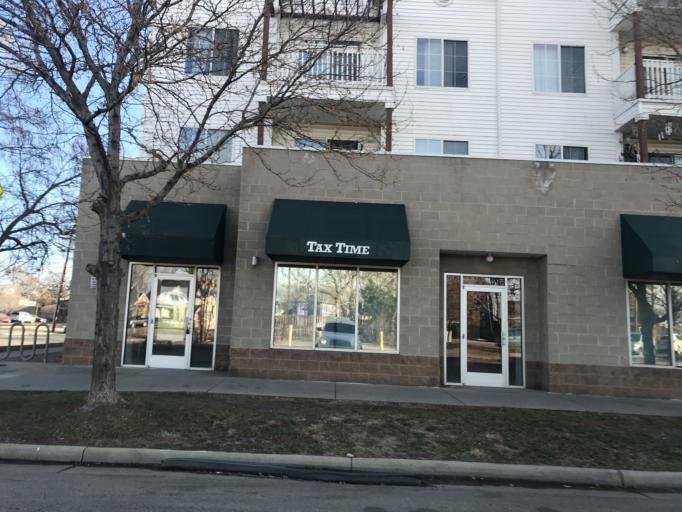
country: US
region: Colorado
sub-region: Denver County
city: Denver
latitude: 39.7631
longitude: -104.9734
